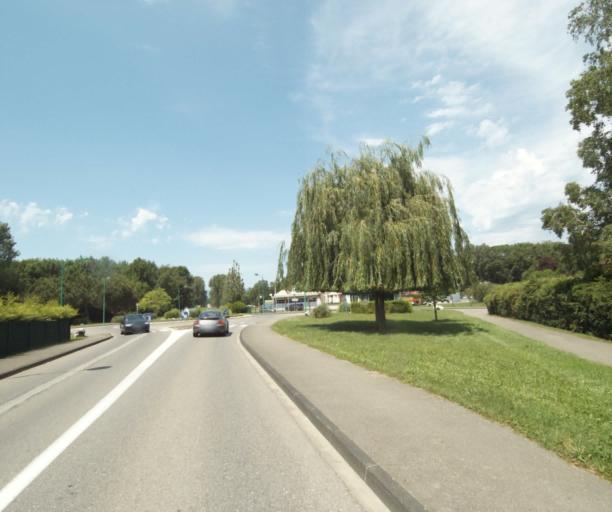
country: FR
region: Rhone-Alpes
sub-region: Departement de la Haute-Savoie
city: Douvaine
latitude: 46.3114
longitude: 6.3010
